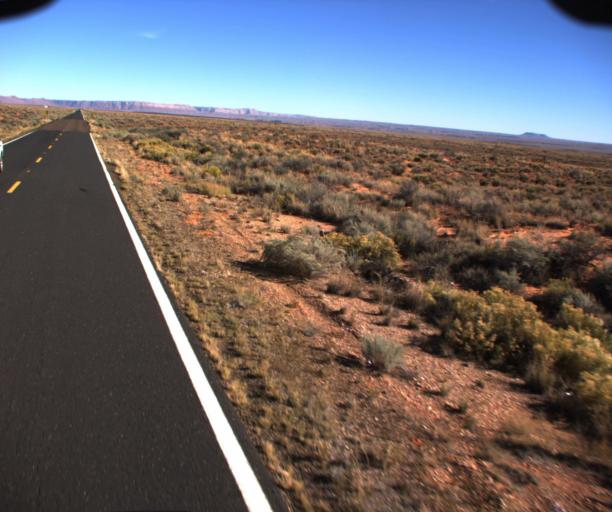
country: US
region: Arizona
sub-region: Coconino County
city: Page
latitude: 36.7012
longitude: -111.9312
